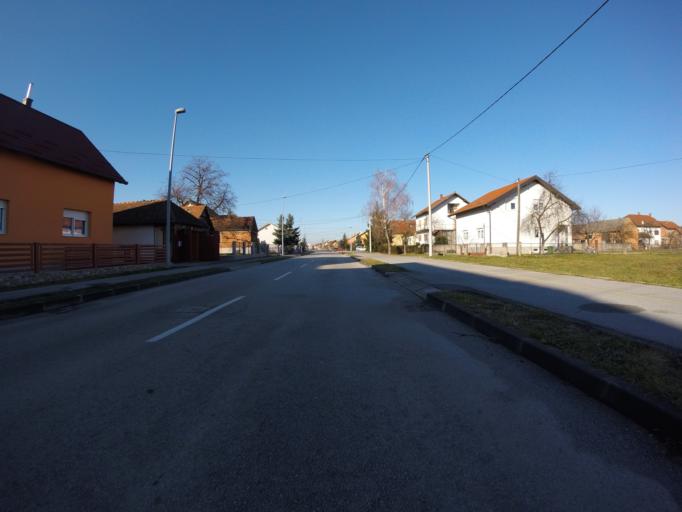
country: HR
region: Zagrebacka
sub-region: Grad Velika Gorica
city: Velika Gorica
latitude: 45.6987
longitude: 16.0710
